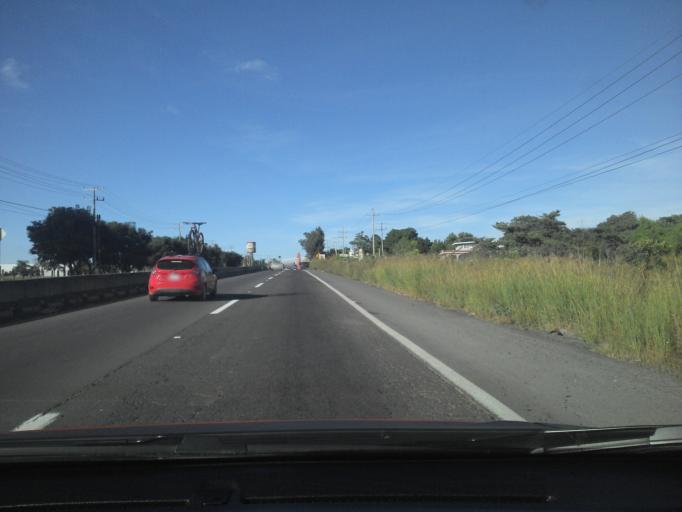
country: MX
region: Jalisco
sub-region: Tala
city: Los Ruisenores
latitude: 20.6988
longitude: -103.6893
